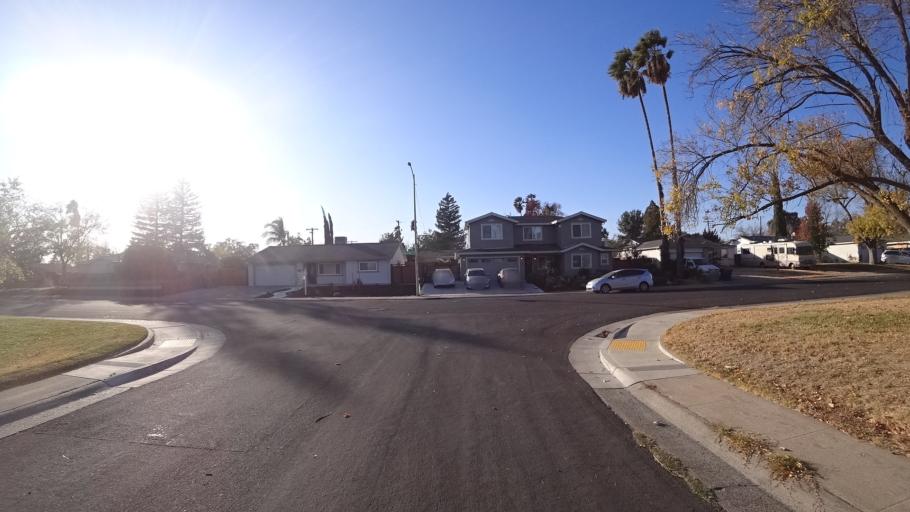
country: US
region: California
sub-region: Sacramento County
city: Citrus Heights
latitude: 38.6982
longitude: -121.2924
